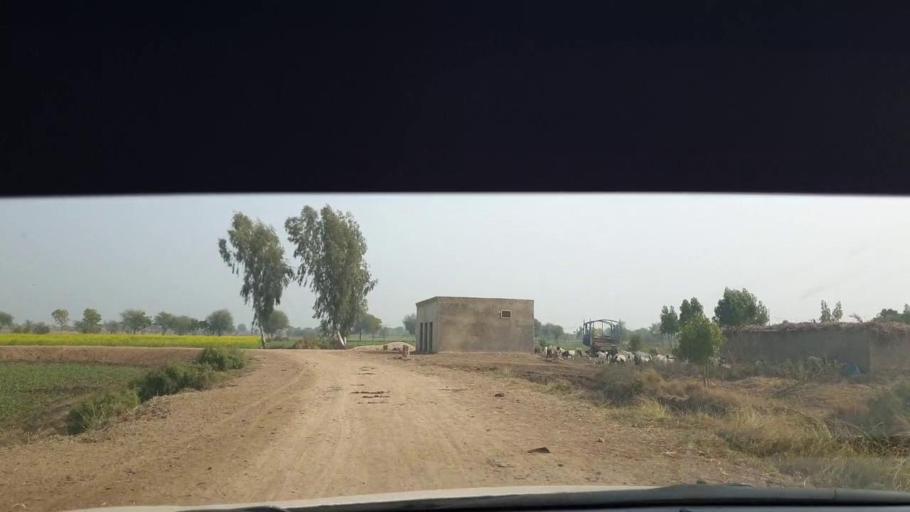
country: PK
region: Sindh
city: Berani
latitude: 25.8281
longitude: 68.8486
